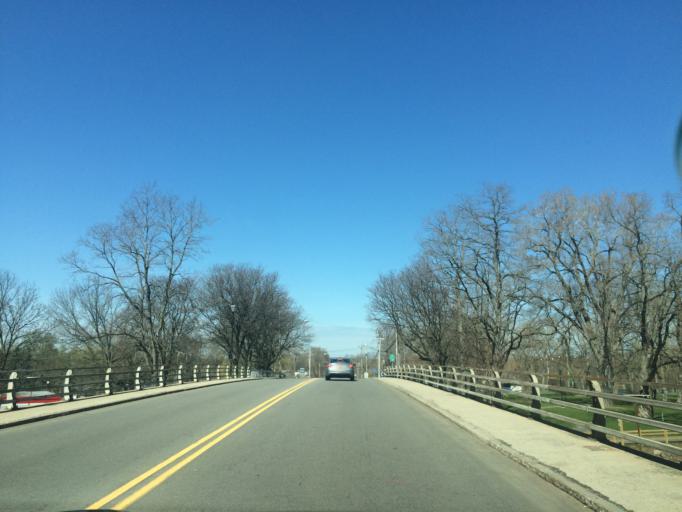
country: US
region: New York
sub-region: Monroe County
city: Fairport
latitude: 43.0999
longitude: -77.4556
